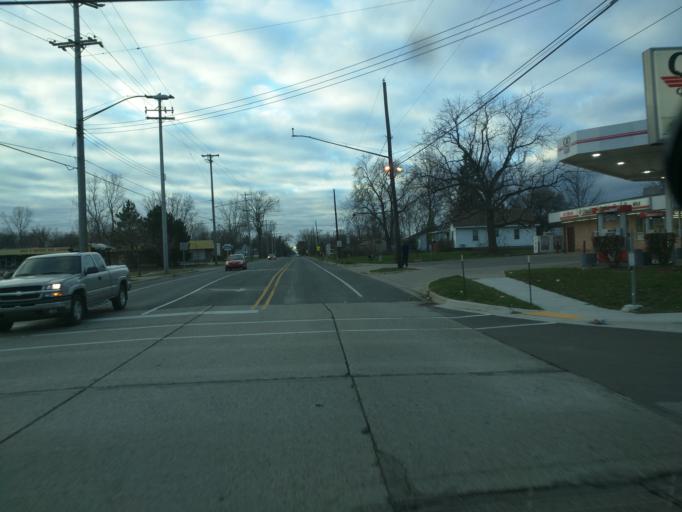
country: US
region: Michigan
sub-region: Eaton County
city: Waverly
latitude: 42.6831
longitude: -84.6031
